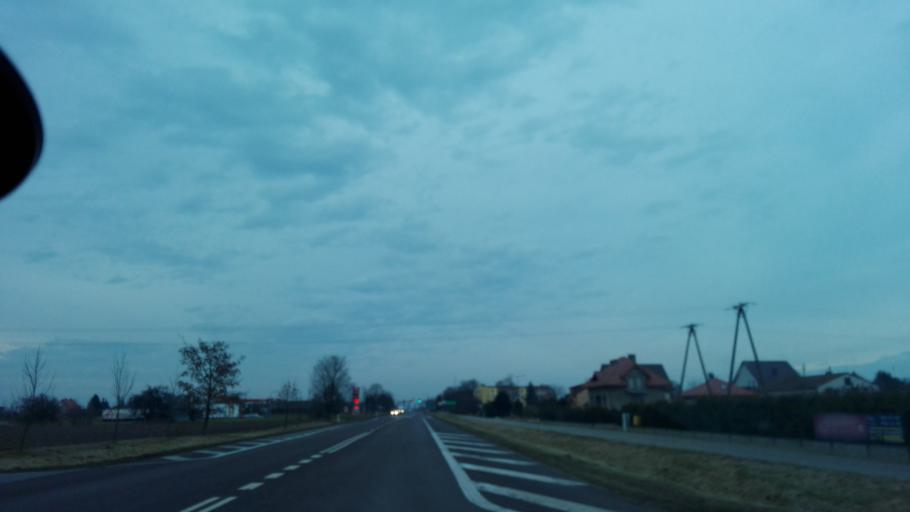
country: PL
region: Lublin Voivodeship
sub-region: Powiat radzynski
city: Radzyn Podlaski
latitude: 51.7789
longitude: 22.5921
